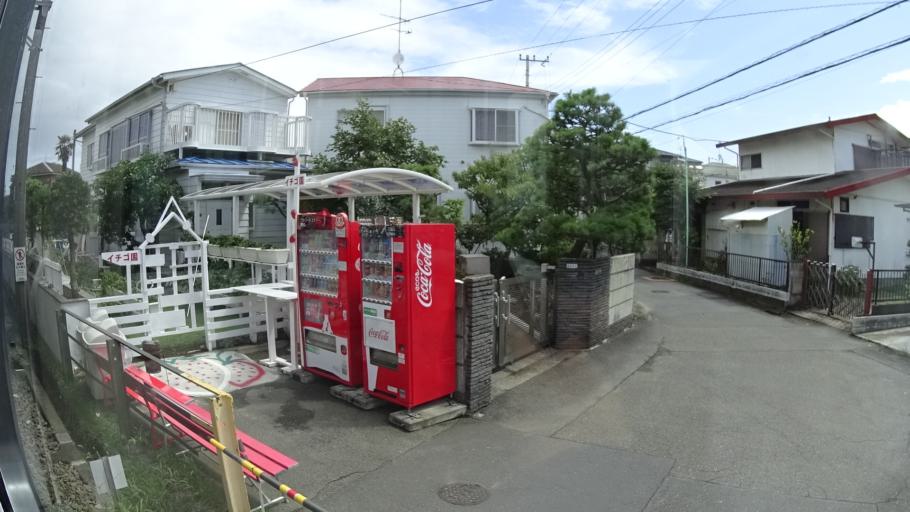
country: JP
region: Kanagawa
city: Fujisawa
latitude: 35.3164
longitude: 139.4820
